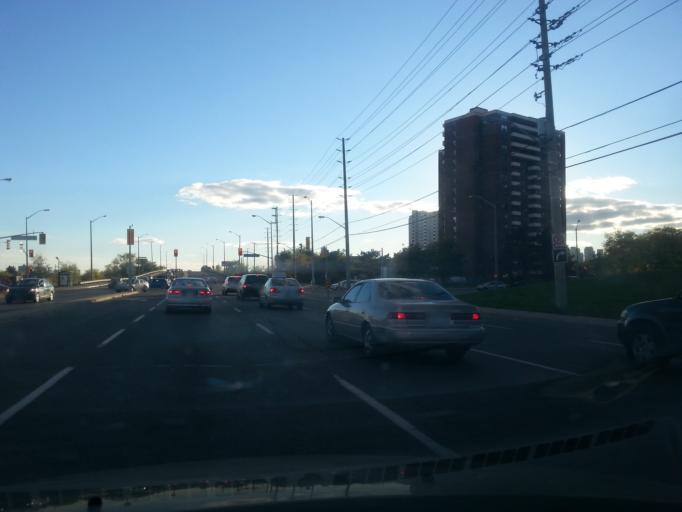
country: CA
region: Ontario
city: Mississauga
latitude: 43.5944
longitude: -79.6005
